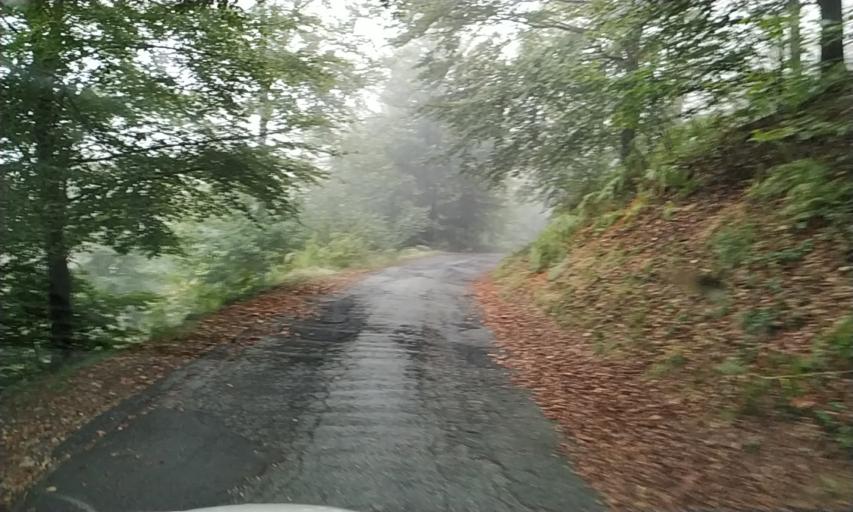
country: IT
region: Piedmont
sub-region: Provincia di Vercelli
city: Civiasco
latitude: 45.8330
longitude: 8.2954
